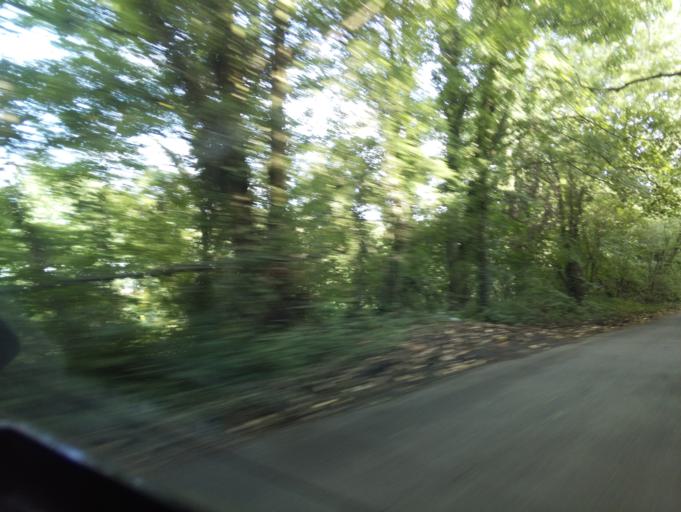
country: GB
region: Wales
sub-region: Caerphilly County Borough
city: Abertridwr
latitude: 51.5671
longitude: -3.2884
